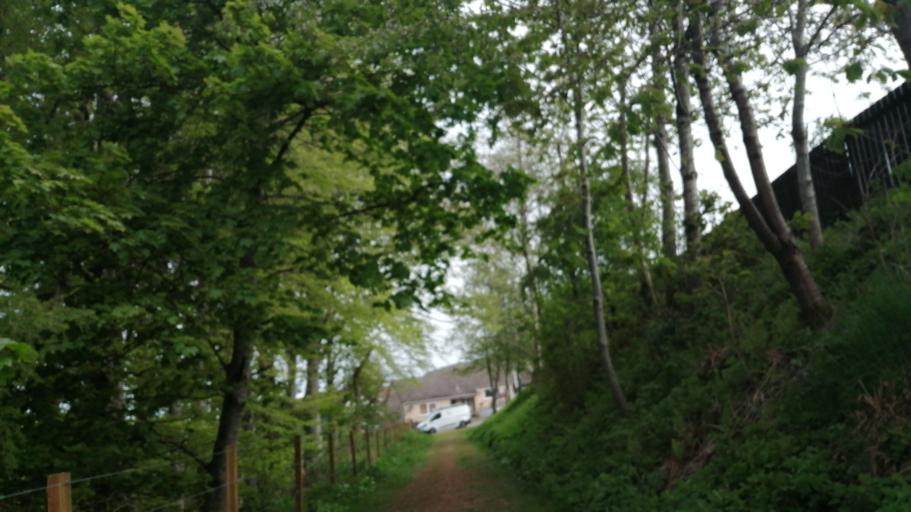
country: GB
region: Scotland
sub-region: Moray
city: Keith
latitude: 57.5377
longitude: -2.9588
